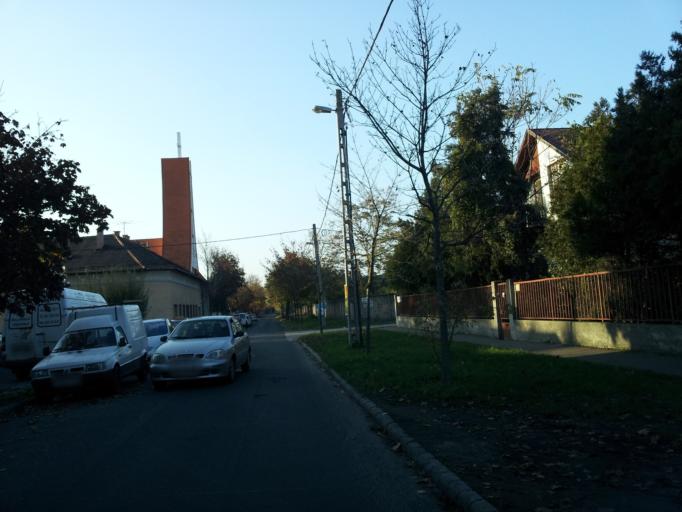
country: HU
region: Budapest
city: Budapest X. keruelet
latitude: 47.4790
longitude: 19.1591
